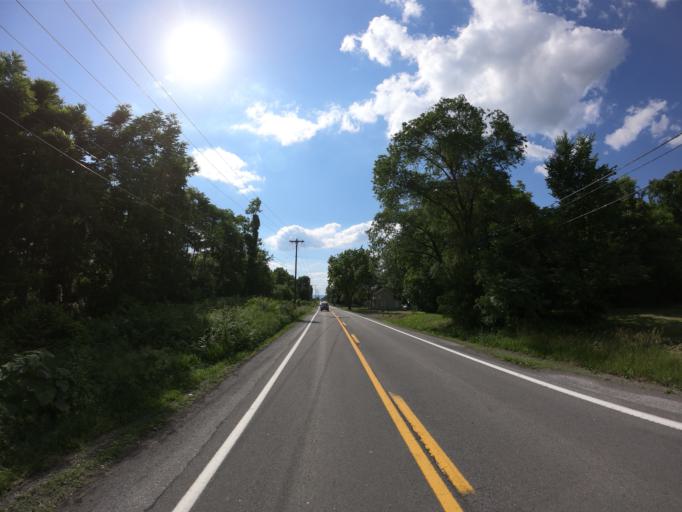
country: US
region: West Virginia
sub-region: Jefferson County
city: Shepherdstown
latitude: 39.3926
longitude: -77.8904
